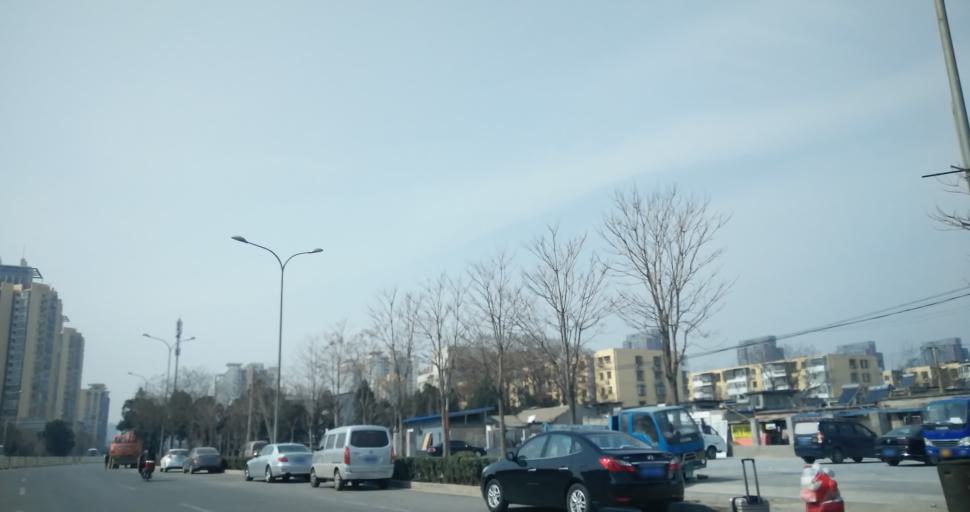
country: CN
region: Beijing
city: Dongfeng
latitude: 39.8597
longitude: 116.5037
